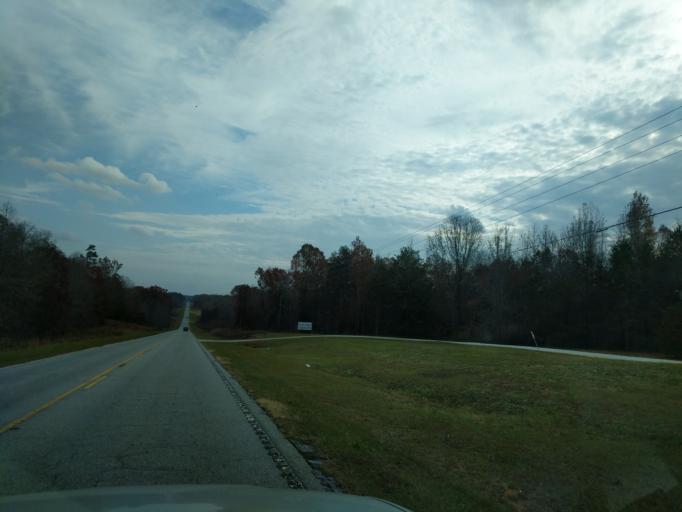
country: US
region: Georgia
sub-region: Franklin County
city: Gumlog
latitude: 34.5266
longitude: -83.0518
